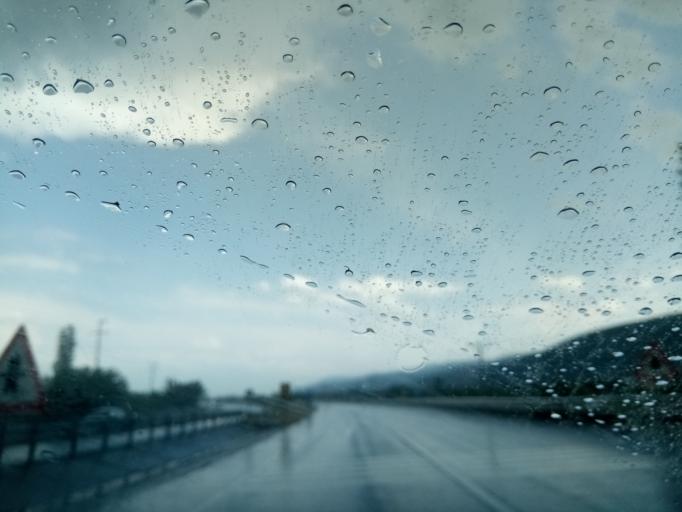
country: TR
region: Afyonkarahisar
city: Sultandagi
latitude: 38.4852
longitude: 31.2796
